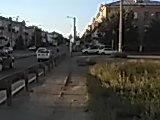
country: RU
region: Orenburg
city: Novotroitsk
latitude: 51.2030
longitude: 58.2991
